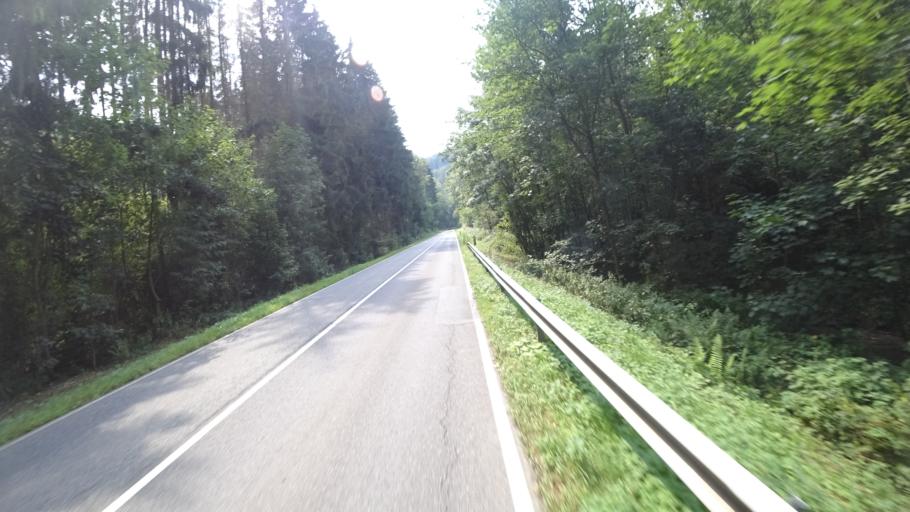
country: DE
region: Rheinland-Pfalz
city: Vallendar
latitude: 50.4218
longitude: 7.6397
